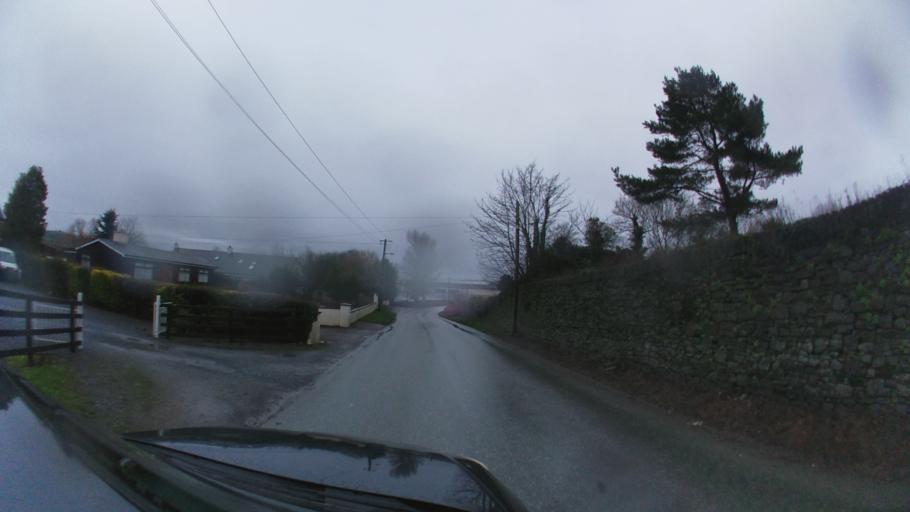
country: IE
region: Leinster
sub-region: County Carlow
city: Bagenalstown
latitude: 52.6333
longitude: -6.9940
